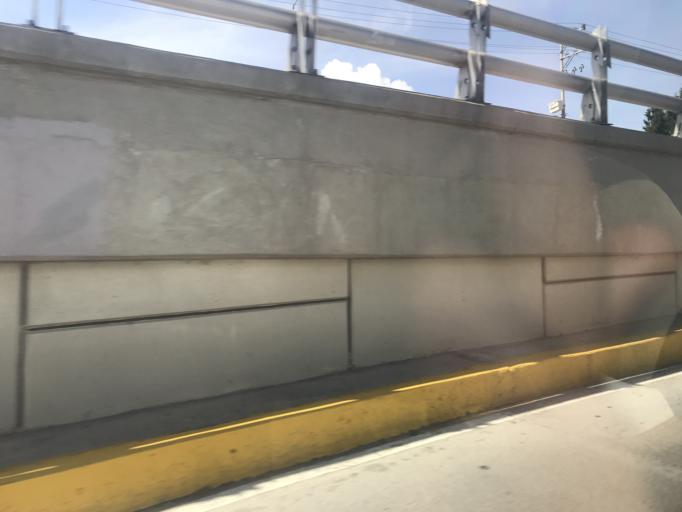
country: MX
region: Puebla
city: Cholula
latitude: 19.0610
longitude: -98.2958
